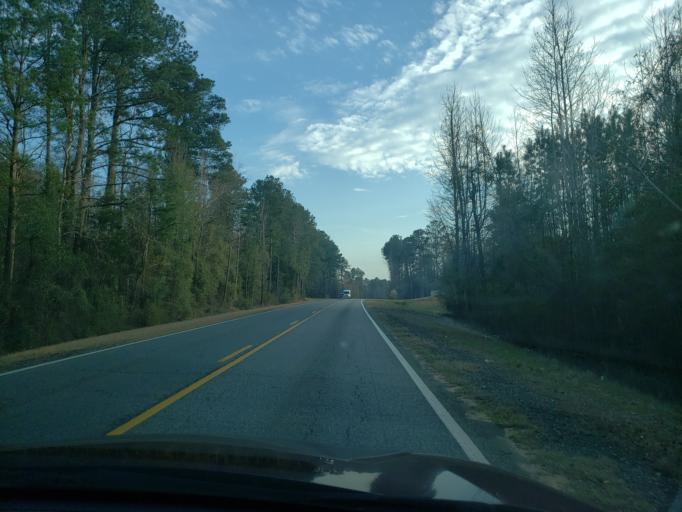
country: US
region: Alabama
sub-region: Hale County
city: Greensboro
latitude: 32.7358
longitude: -87.5860
